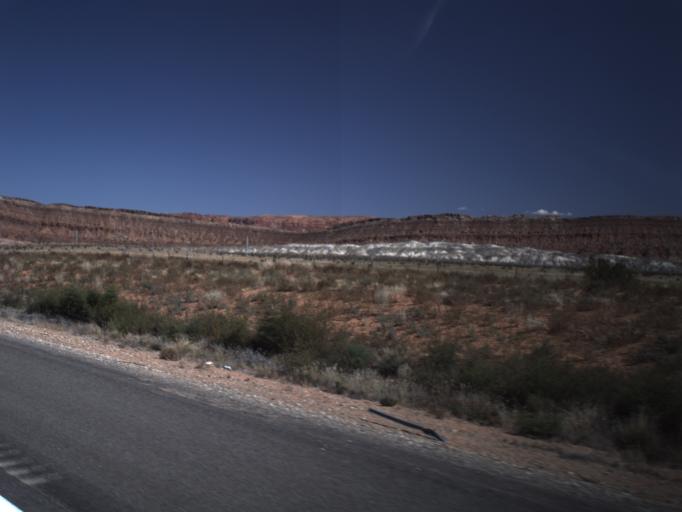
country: US
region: Utah
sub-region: Washington County
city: Washington
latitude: 37.0243
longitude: -113.4857
